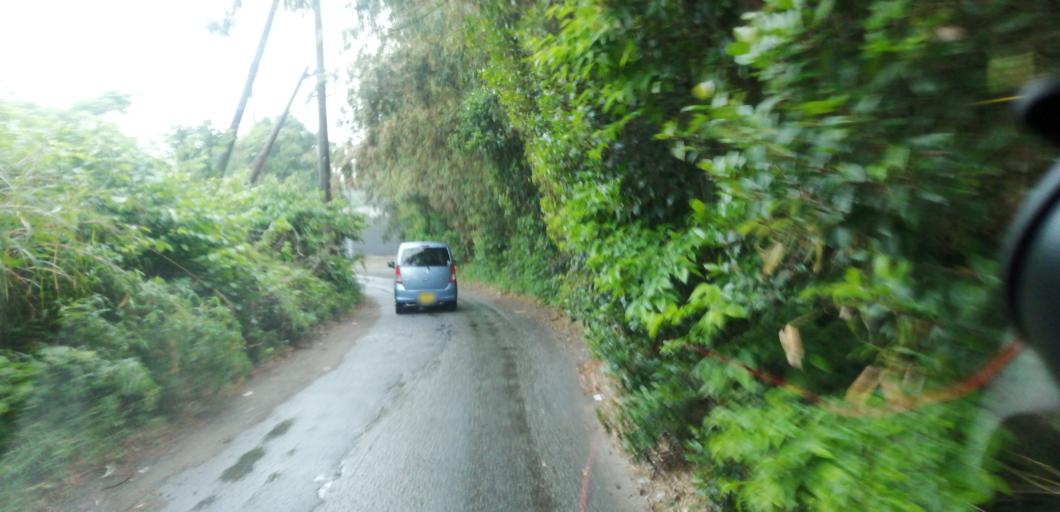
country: JP
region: Chiba
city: Ichihara
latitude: 35.4825
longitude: 140.1469
